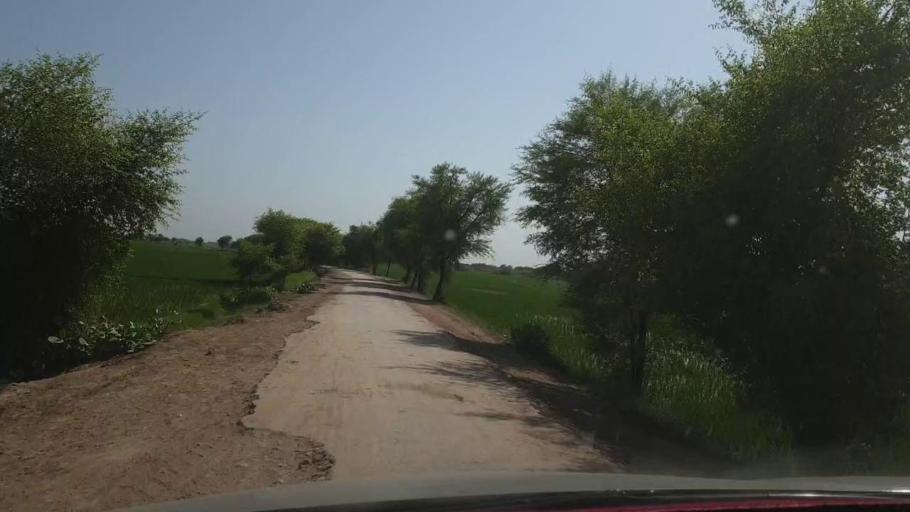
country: PK
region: Sindh
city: Nasirabad
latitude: 27.3525
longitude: 67.8434
